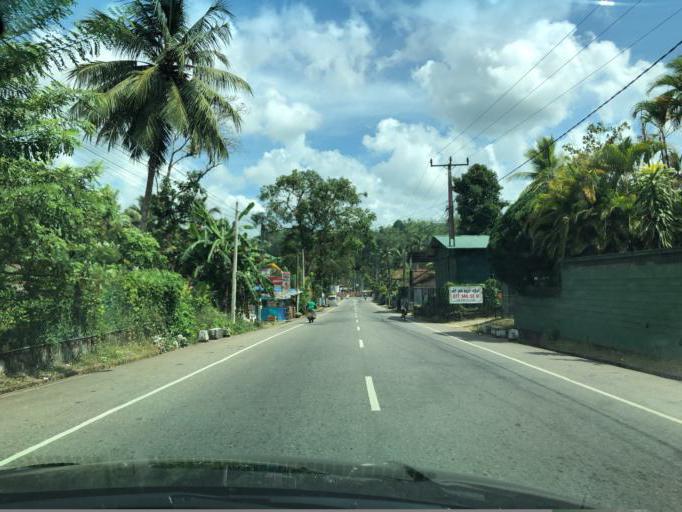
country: LK
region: Western
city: Horawala Junction
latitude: 6.5255
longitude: 80.1040
